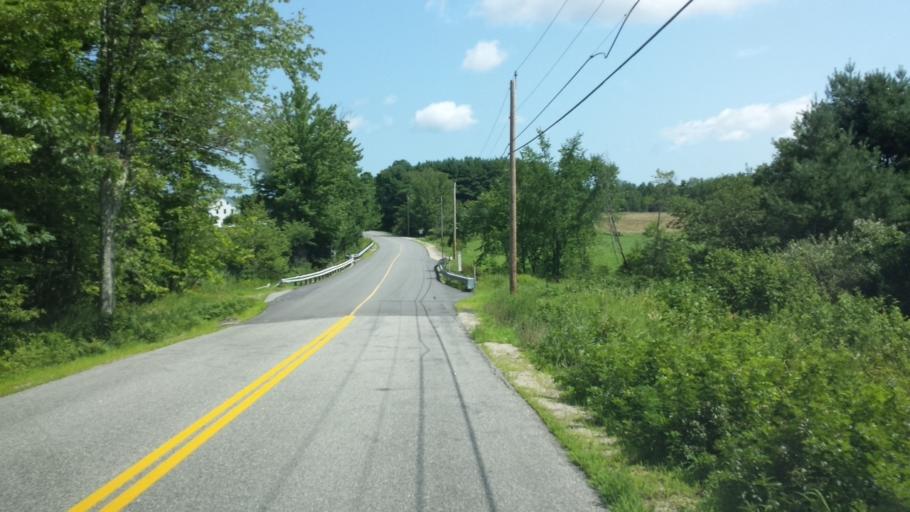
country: US
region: Maine
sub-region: York County
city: West Kennebunk
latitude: 43.4316
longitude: -70.5537
